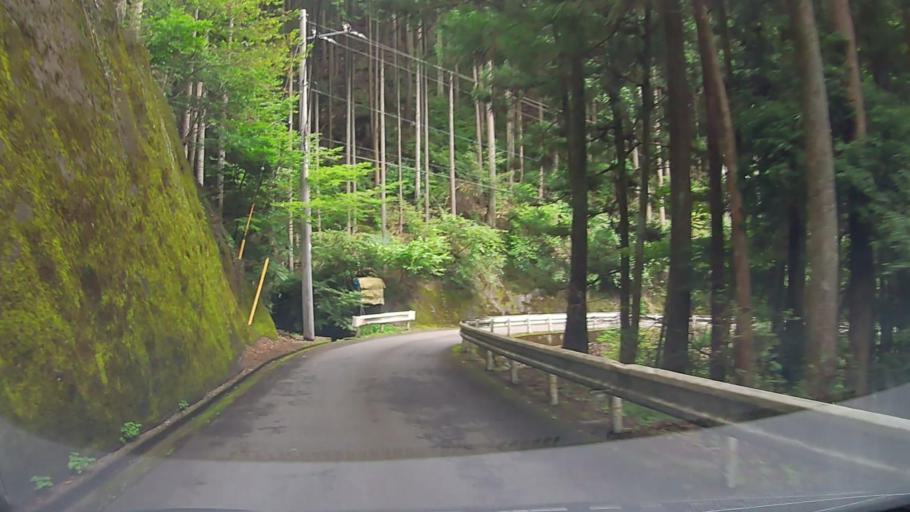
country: JP
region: Yamanashi
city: Uenohara
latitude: 35.7455
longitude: 139.0807
